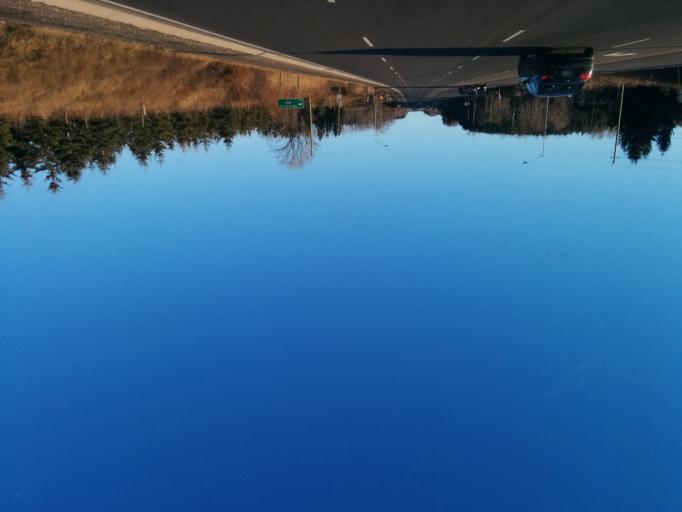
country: CA
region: Ontario
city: Orangeville
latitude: 43.8318
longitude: -79.9572
